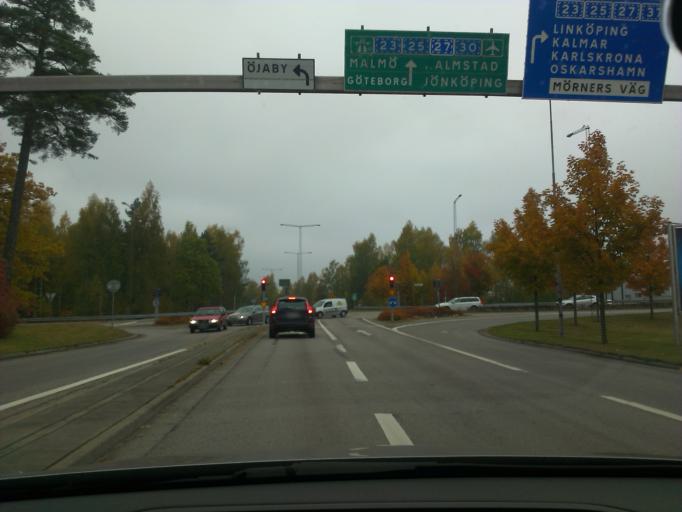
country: SE
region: Kronoberg
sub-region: Vaxjo Kommun
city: Vaexjoe
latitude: 56.8845
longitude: 14.7617
